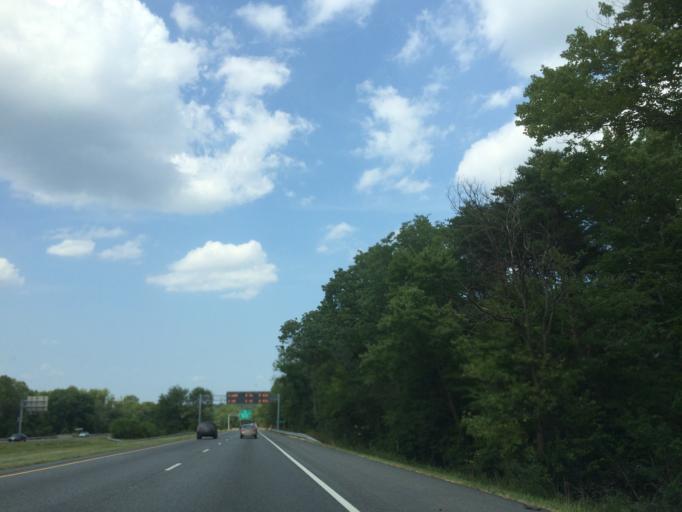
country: US
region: Maryland
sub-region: Howard County
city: Hanover
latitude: 39.1860
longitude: -76.7164
